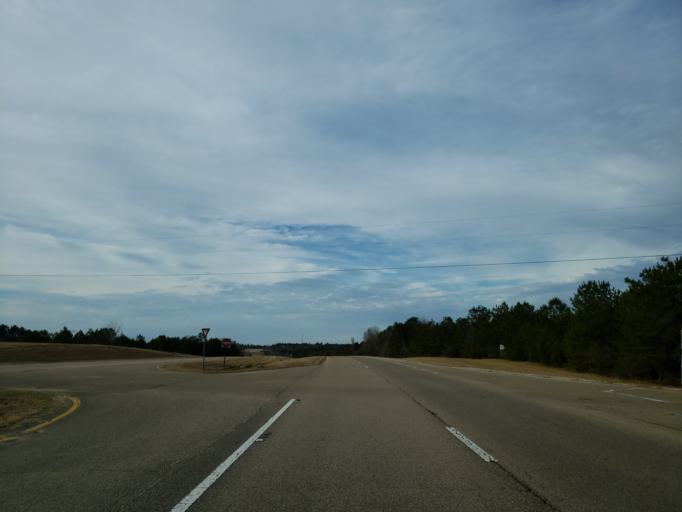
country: US
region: Mississippi
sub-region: Wayne County
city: Waynesboro
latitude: 31.6678
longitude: -88.6052
